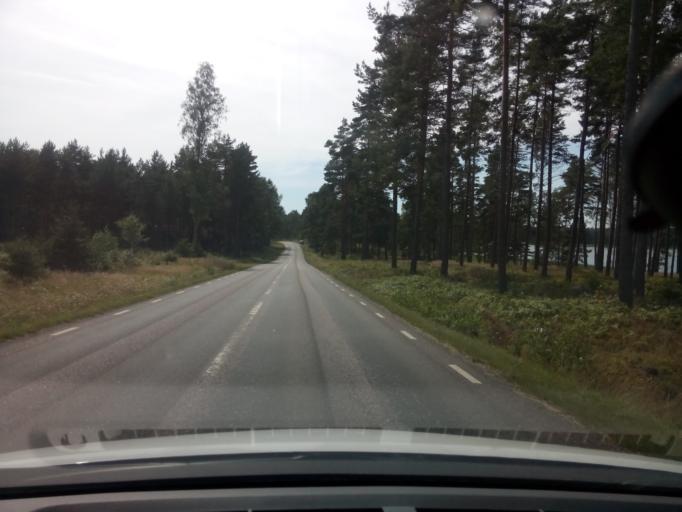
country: SE
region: Soedermanland
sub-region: Oxelosunds Kommun
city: Oxelosund
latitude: 58.7637
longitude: 17.3317
